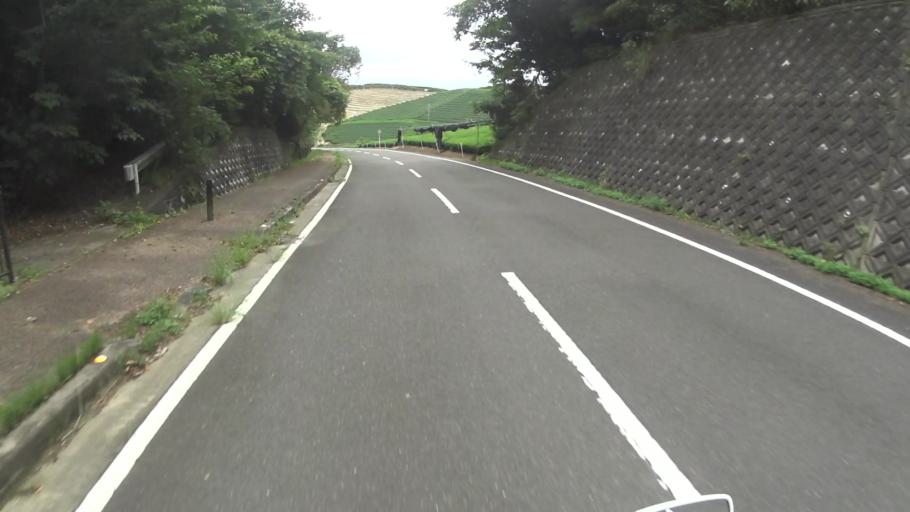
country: JP
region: Kyoto
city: Uji
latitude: 34.8055
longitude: 135.8949
